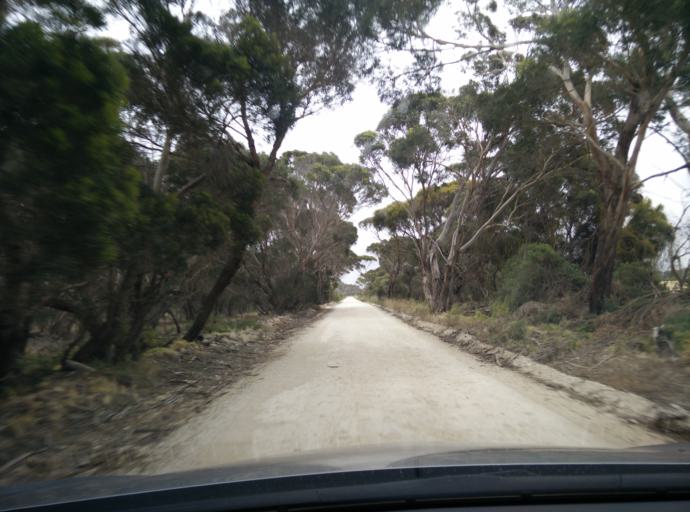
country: AU
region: South Australia
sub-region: Kangaroo Island
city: Kingscote
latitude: -35.8488
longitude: 137.5563
